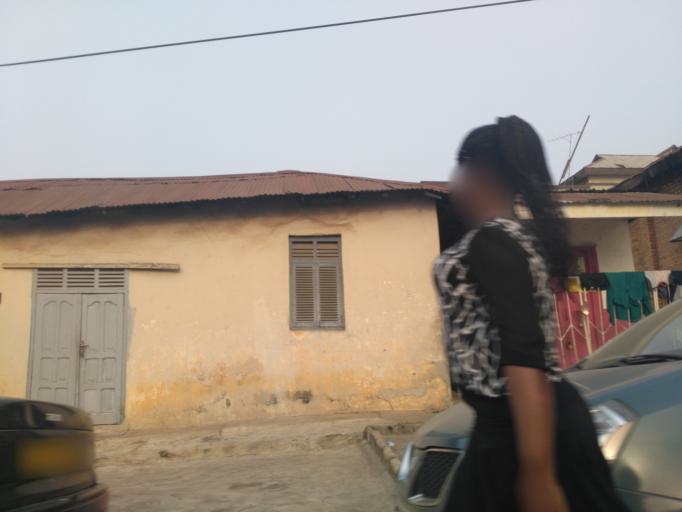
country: GH
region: Ashanti
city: Kumasi
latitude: 6.6881
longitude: -1.6141
